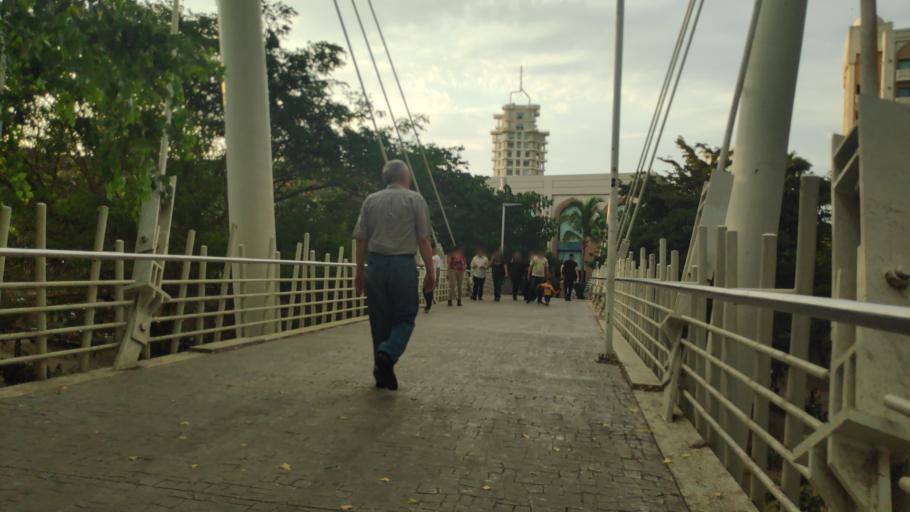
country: MX
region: Sinaloa
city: Culiacan
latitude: 24.8130
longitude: -107.3988
